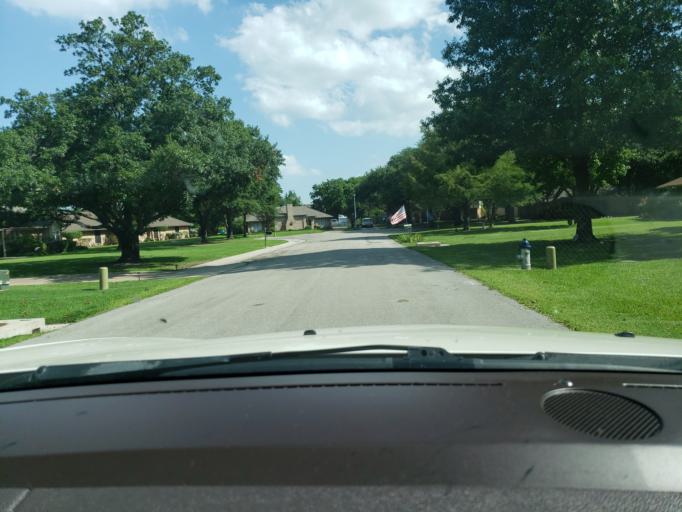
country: US
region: Texas
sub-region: Dallas County
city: Rowlett
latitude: 32.8925
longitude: -96.5731
